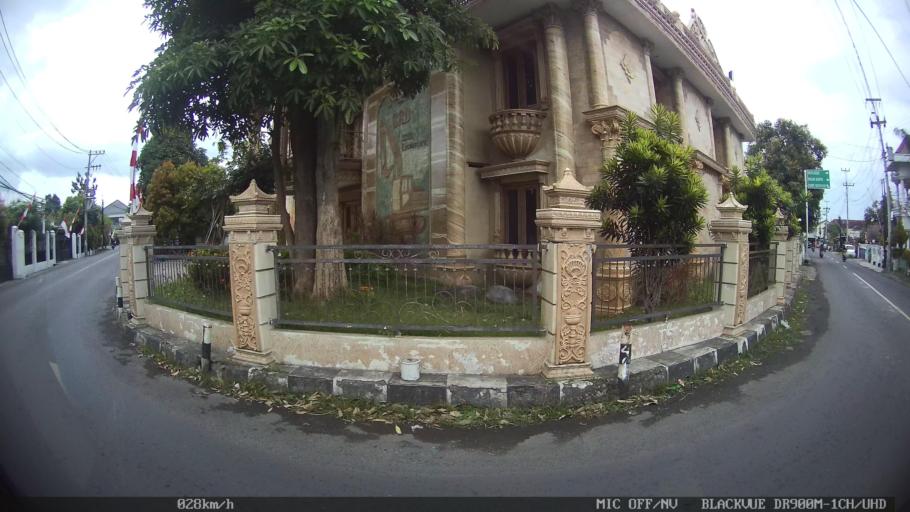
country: ID
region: Daerah Istimewa Yogyakarta
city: Depok
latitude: -7.8282
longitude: 110.4124
